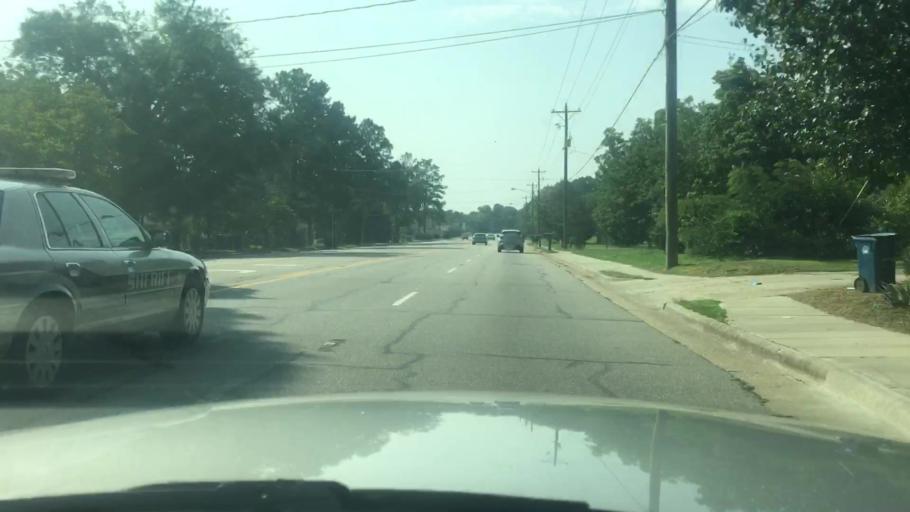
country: US
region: North Carolina
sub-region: Cumberland County
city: Vander
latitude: 35.0190
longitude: -78.8394
